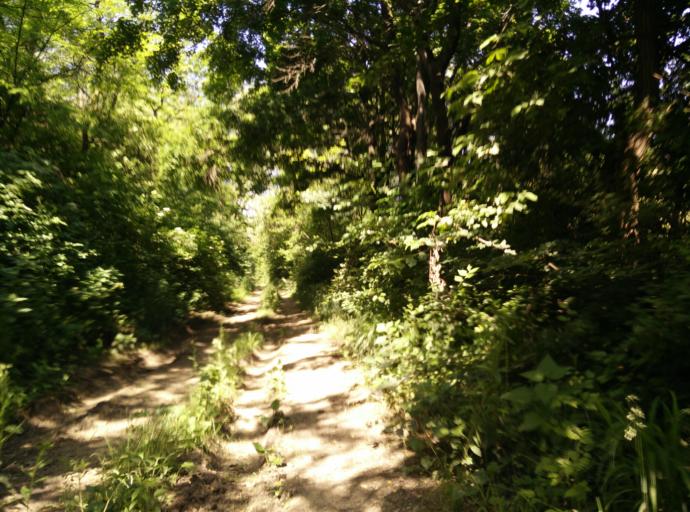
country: HU
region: Pest
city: Biatorbagy
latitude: 47.4708
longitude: 18.8510
